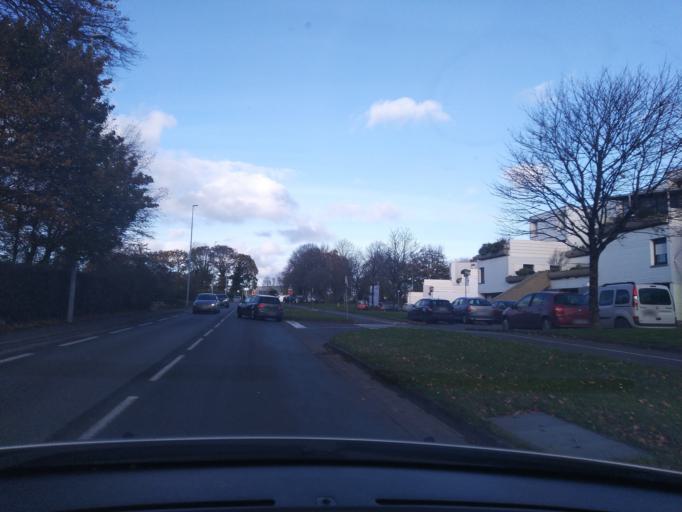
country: FR
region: Brittany
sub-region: Departement du Finistere
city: Morlaix
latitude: 48.5858
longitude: -3.8153
